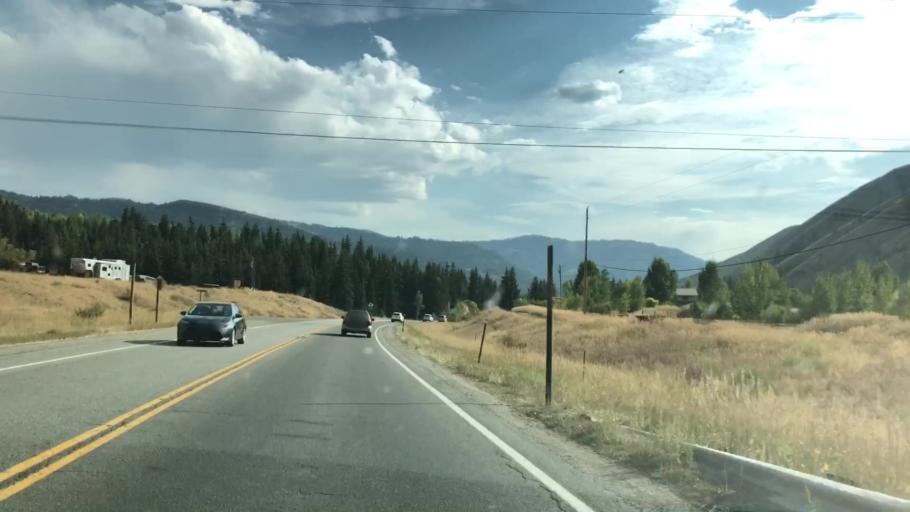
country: US
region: Wyoming
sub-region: Teton County
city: Hoback
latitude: 43.3430
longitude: -110.7223
